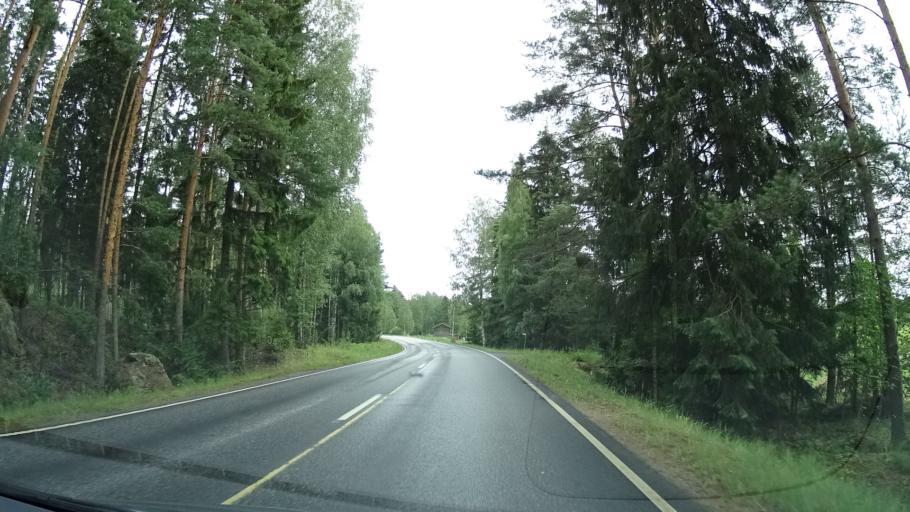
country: FI
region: Haeme
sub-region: Forssa
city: Humppila
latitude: 61.0937
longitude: 23.3707
